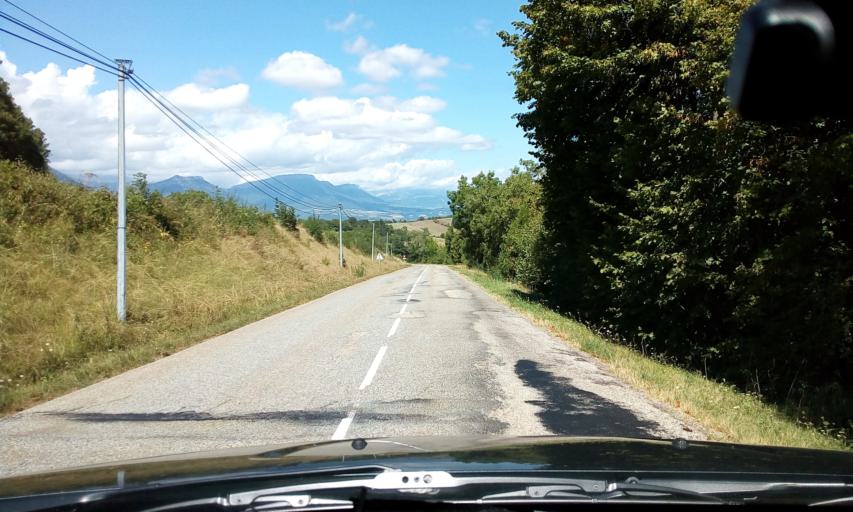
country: FR
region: Rhone-Alpes
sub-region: Departement de l'Isere
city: Mens
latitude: 44.7519
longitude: 5.6769
